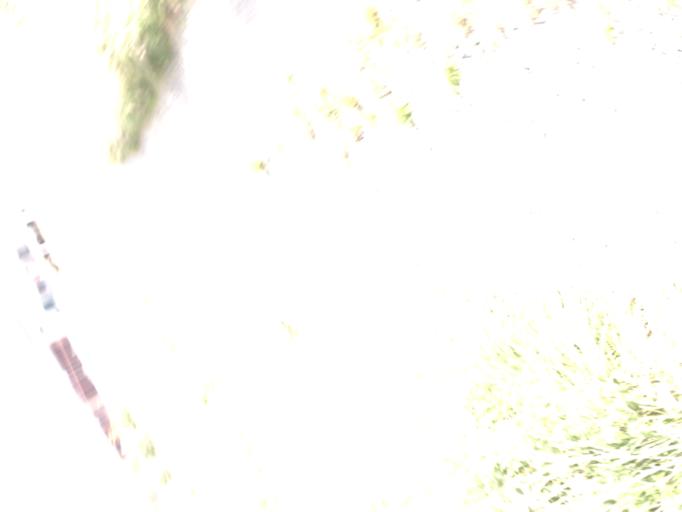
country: SE
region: Vaestra Goetaland
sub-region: Goteborg
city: Majorna
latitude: 57.7410
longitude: 11.8613
